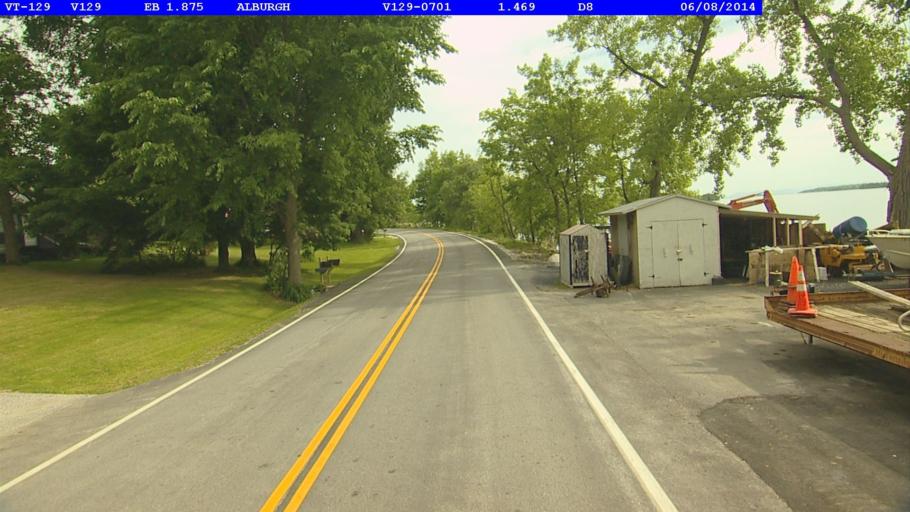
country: US
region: Vermont
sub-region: Grand Isle County
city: North Hero
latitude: 44.8900
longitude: -73.3038
